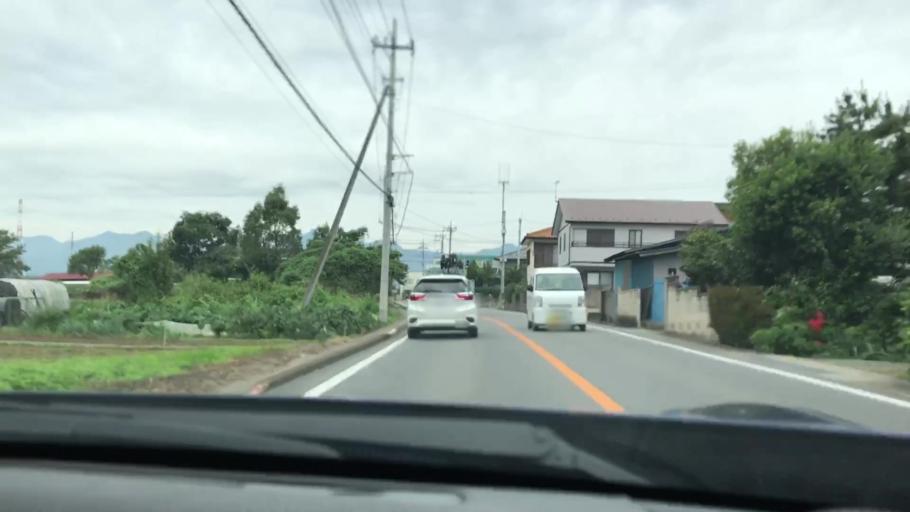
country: JP
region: Gunma
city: Kanekomachi
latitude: 36.3980
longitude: 138.9922
